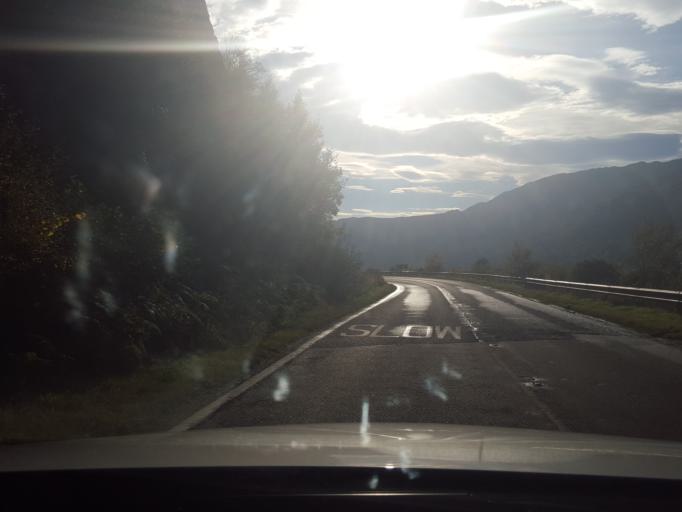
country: GB
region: Scotland
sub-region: Highland
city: Fort William
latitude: 57.2690
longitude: -5.5070
